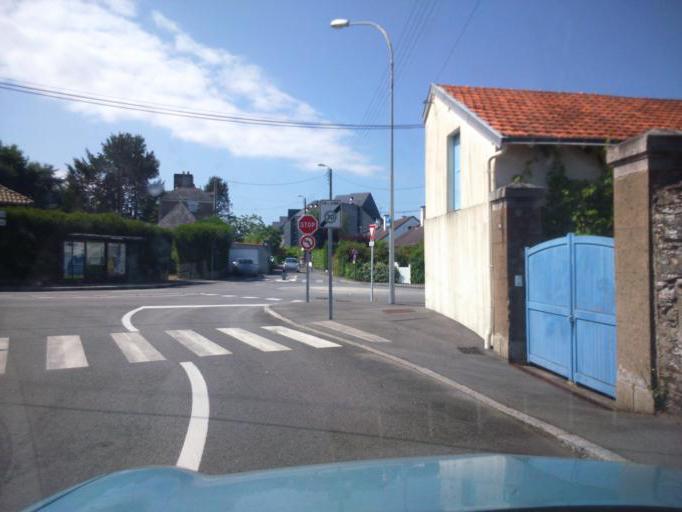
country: FR
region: Pays de la Loire
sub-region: Departement de la Loire-Atlantique
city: Saint-Sebastien-sur-Loire
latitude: 47.2023
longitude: -1.5227
